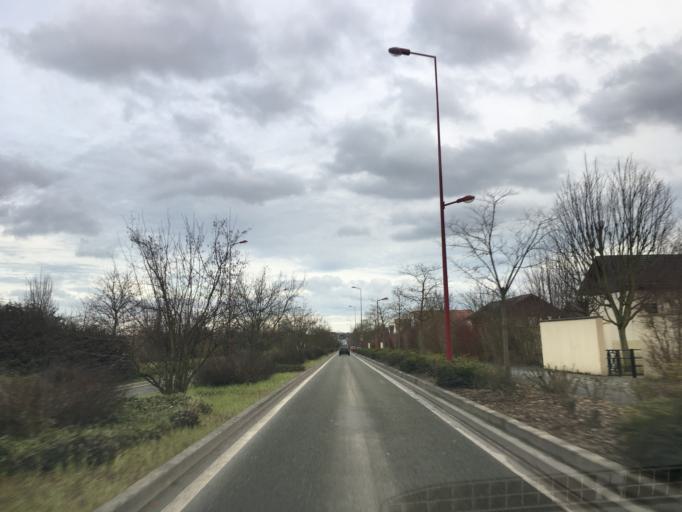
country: FR
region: Ile-de-France
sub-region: Departement du Val-d'Oise
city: Gonesse
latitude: 49.0005
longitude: 2.4316
